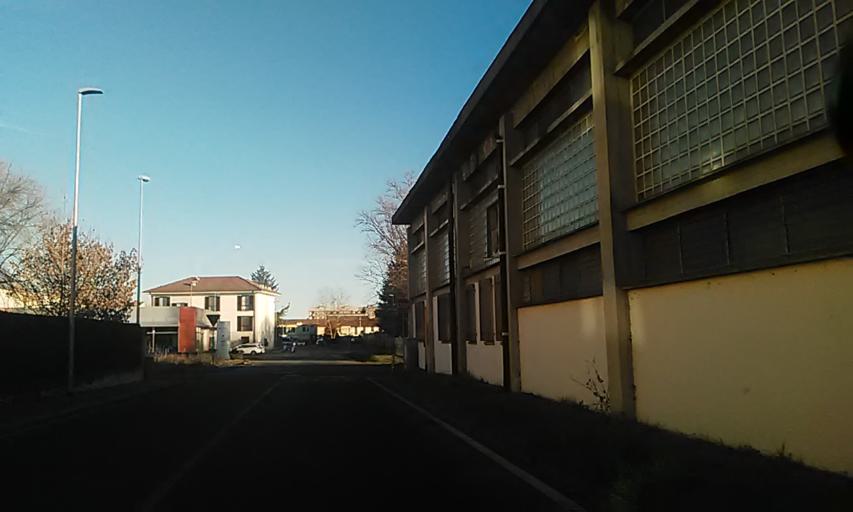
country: IT
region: Piedmont
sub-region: Provincia di Vercelli
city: Vercelli
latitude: 45.3257
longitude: 8.3981
